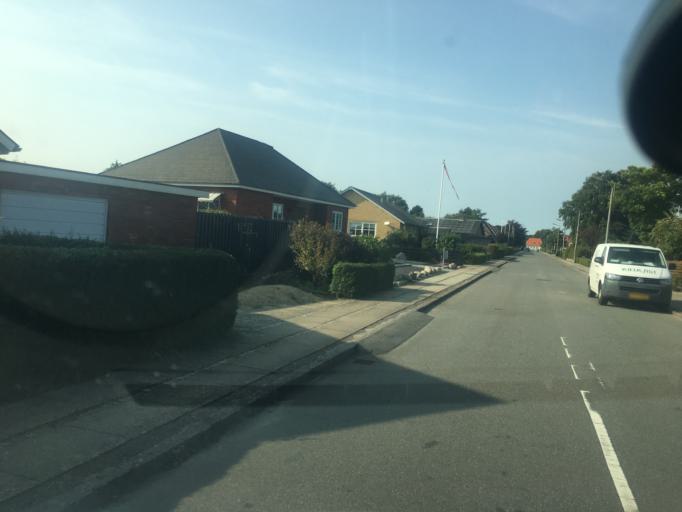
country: DK
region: South Denmark
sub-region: Tonder Kommune
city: Tonder
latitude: 54.9395
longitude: 8.8682
